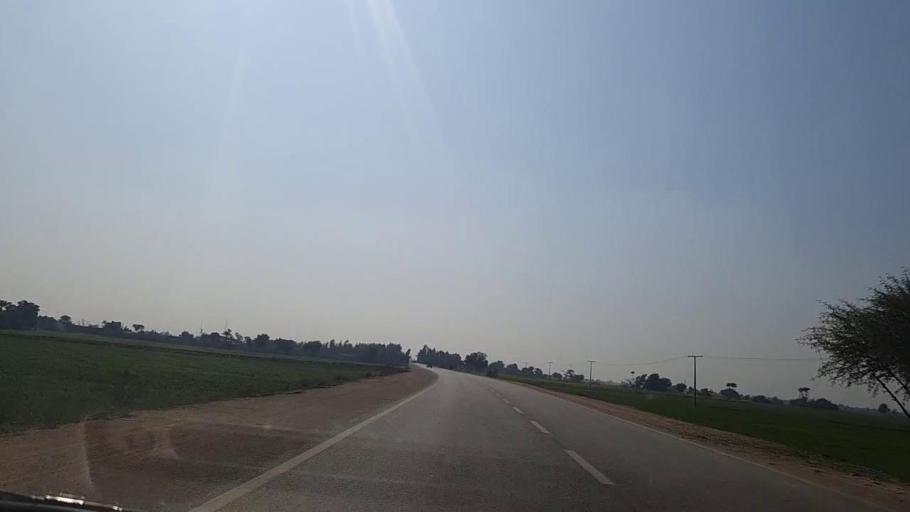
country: PK
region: Sindh
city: Hala
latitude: 25.9901
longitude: 68.3879
